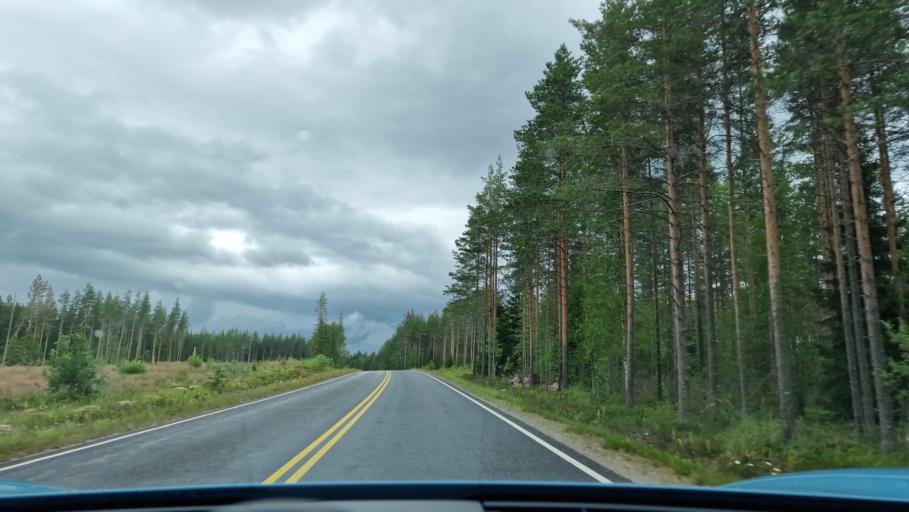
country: FI
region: Southern Ostrobothnia
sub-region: Jaerviseutu
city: Soini
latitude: 62.7466
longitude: 24.4089
